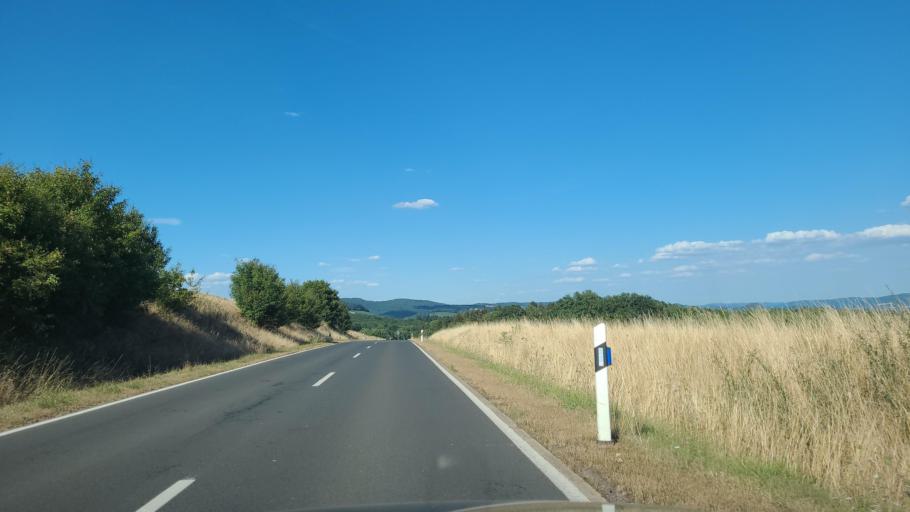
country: DE
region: Rheinland-Pfalz
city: Bergweiler
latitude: 49.9737
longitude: 6.8385
